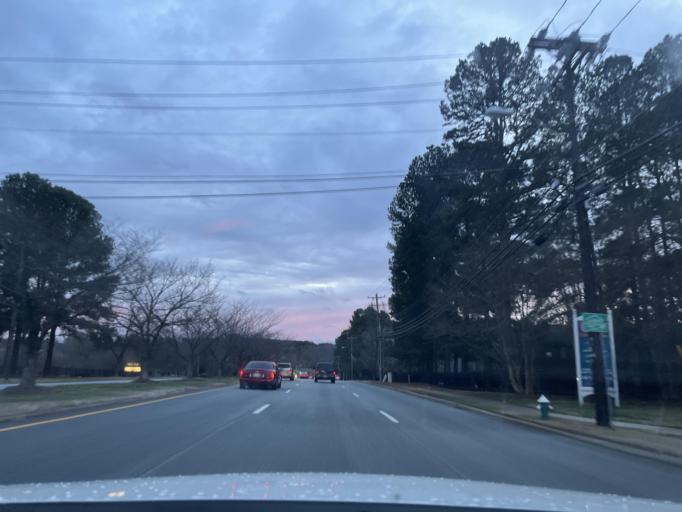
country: US
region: North Carolina
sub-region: Guilford County
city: Greensboro
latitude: 36.0357
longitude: -79.8500
